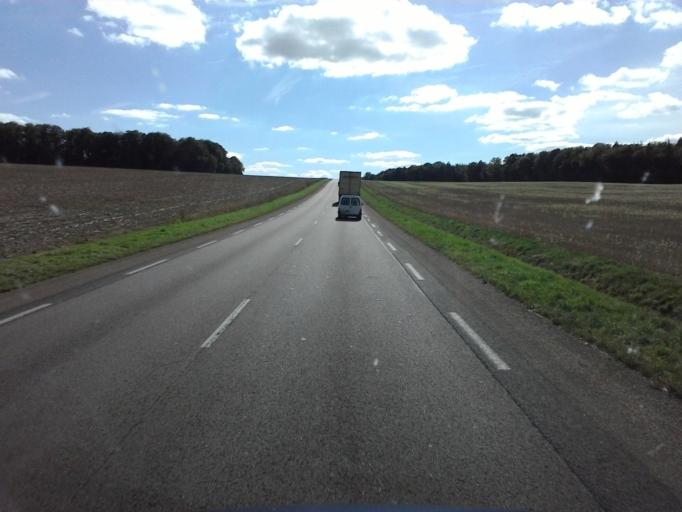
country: FR
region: Bourgogne
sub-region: Departement de la Cote-d'Or
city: Chatillon-sur-Seine
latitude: 47.7895
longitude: 4.5144
